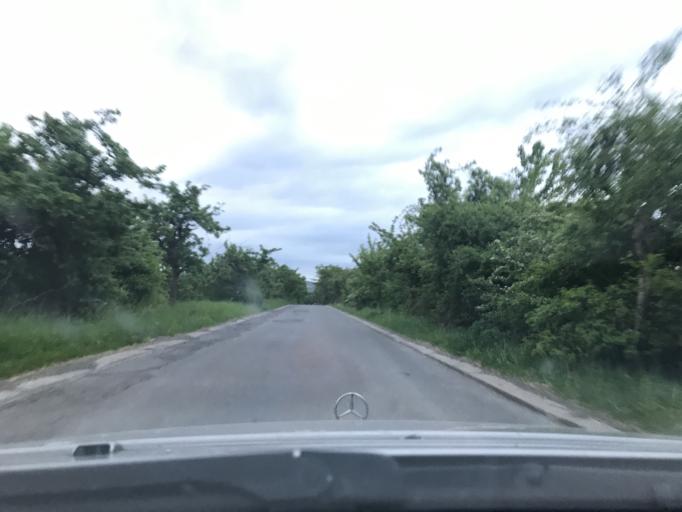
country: DE
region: Thuringia
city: Muehlhausen
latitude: 51.2224
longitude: 10.4116
